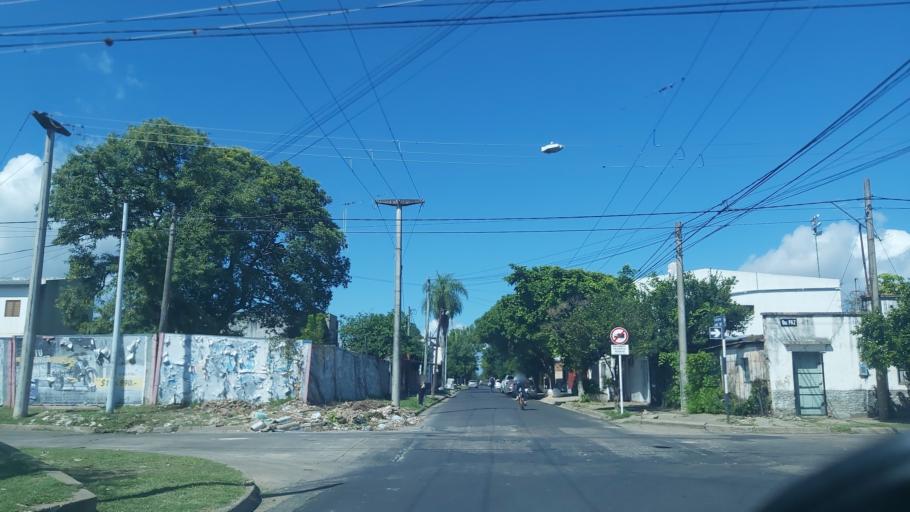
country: AR
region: Corrientes
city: Corrientes
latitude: -27.4767
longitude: -58.8472
